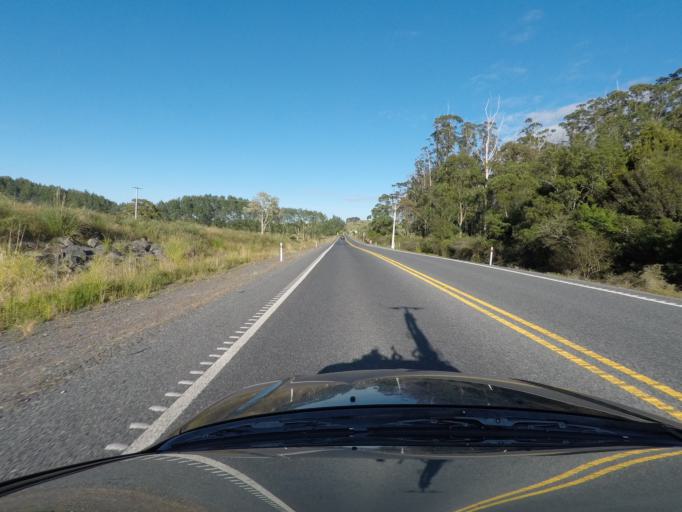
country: NZ
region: Northland
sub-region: Far North District
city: Kawakawa
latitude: -35.4959
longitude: 174.1590
